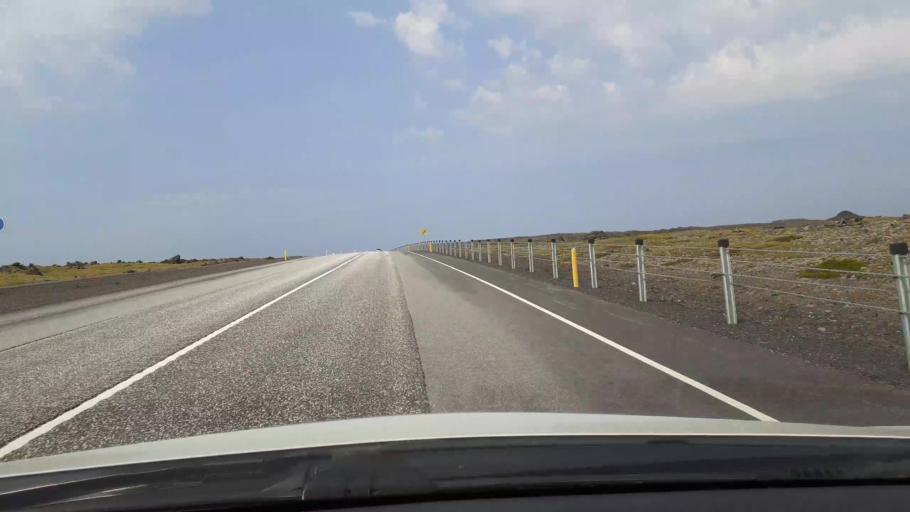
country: IS
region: Southern Peninsula
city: Grindavik
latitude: 63.8964
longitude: -22.4214
